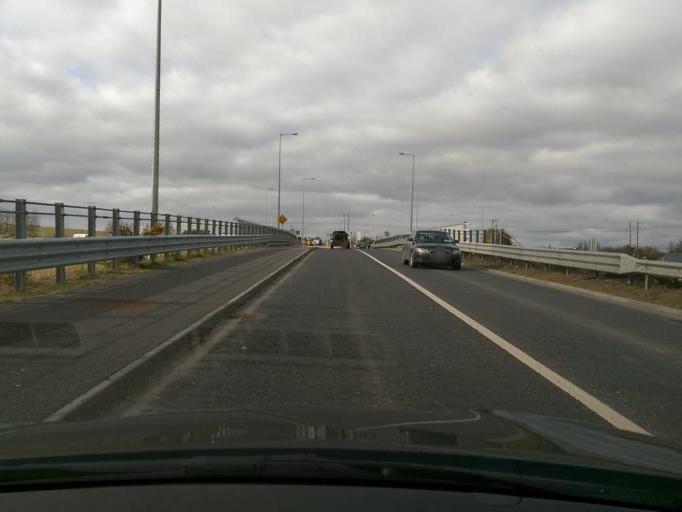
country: IE
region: Leinster
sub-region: An Iarmhi
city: Athlone
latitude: 53.4187
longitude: -7.9758
